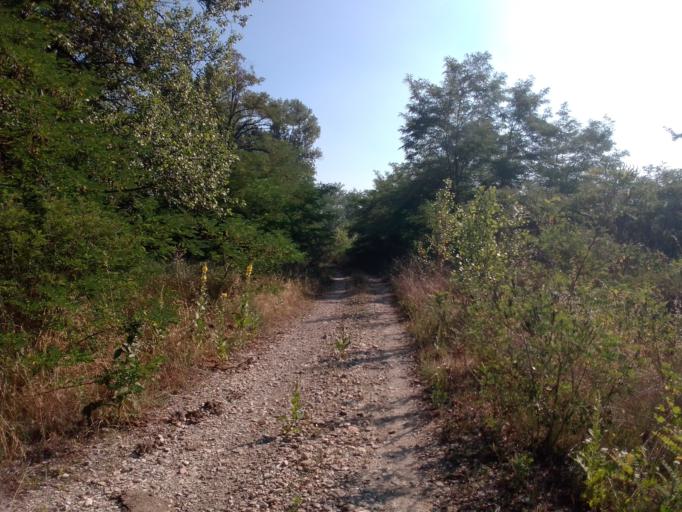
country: IT
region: Emilia-Romagna
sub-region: Provincia di Piacenza
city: Borgonovo Valtidone
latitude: 44.9942
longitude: 9.4806
